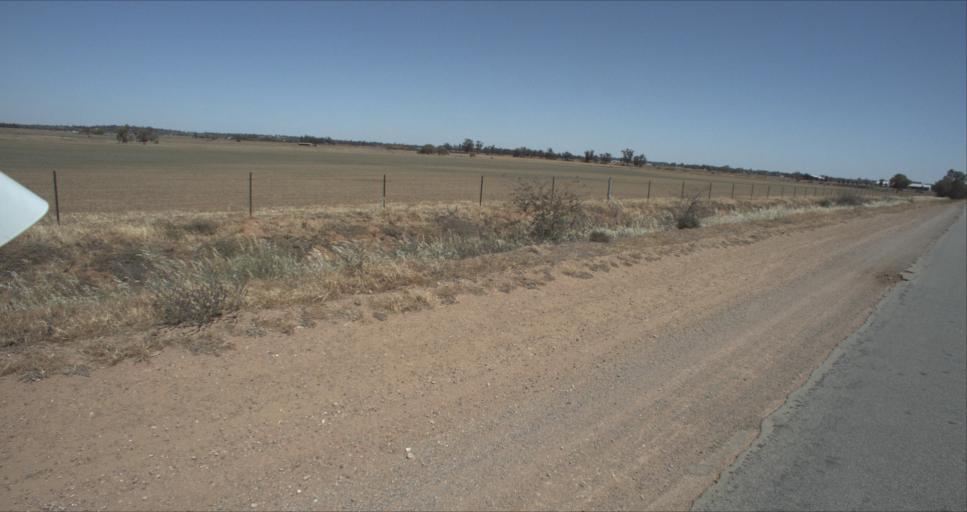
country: AU
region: New South Wales
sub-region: Leeton
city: Leeton
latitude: -34.5401
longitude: 146.4399
